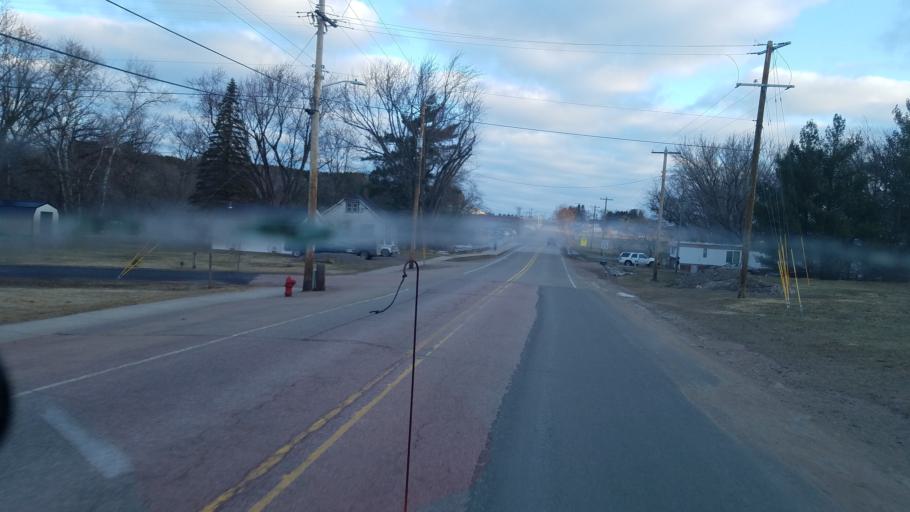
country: US
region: Wisconsin
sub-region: Clark County
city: Neillsville
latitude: 44.5892
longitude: -90.4614
